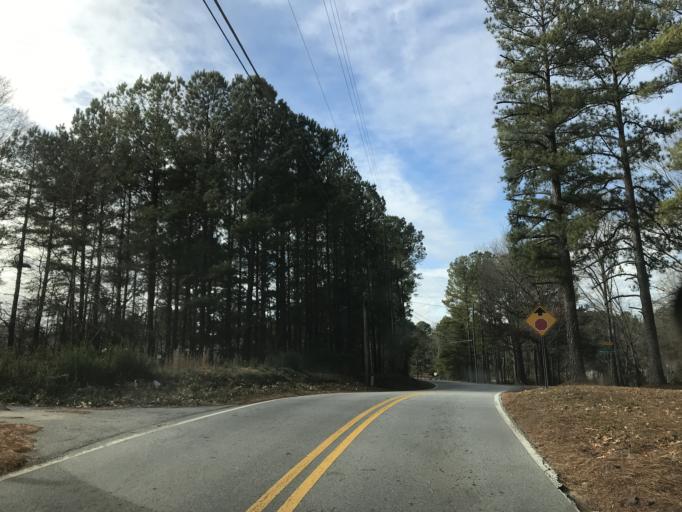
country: US
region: Georgia
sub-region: Douglas County
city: Douglasville
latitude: 33.7960
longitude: -84.8281
